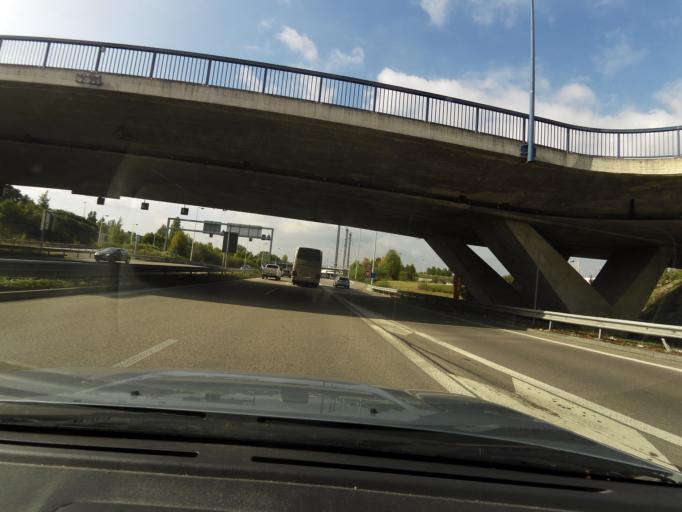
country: FR
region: Alsace
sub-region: Departement du Haut-Rhin
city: Saint-Louis
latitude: 47.5750
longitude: 7.5639
